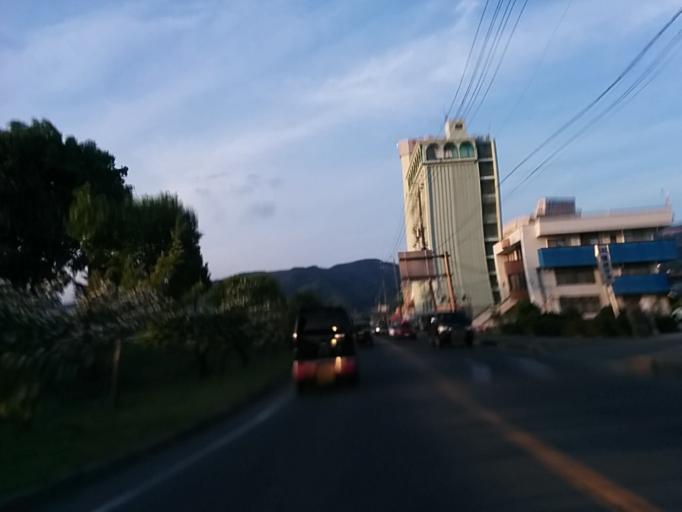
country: JP
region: Nagano
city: Suwa
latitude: 36.0408
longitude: 138.1037
